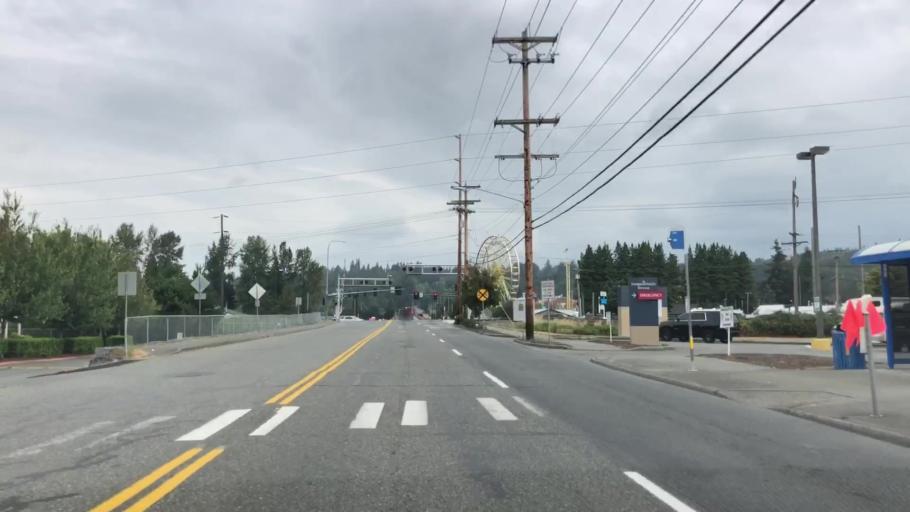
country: US
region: Washington
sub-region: Snohomish County
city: Monroe
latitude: 47.8643
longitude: -121.9907
